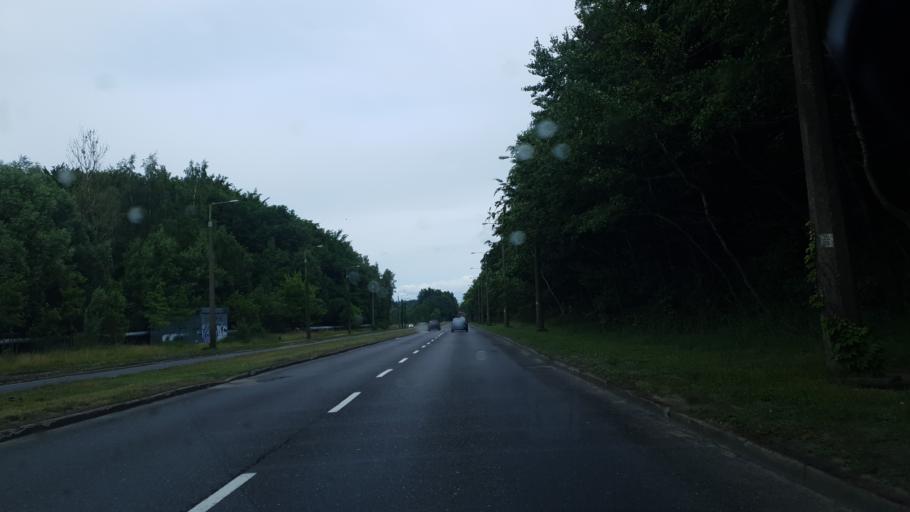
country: PL
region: Pomeranian Voivodeship
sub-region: Gdynia
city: Wielki Kack
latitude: 54.4652
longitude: 18.4661
